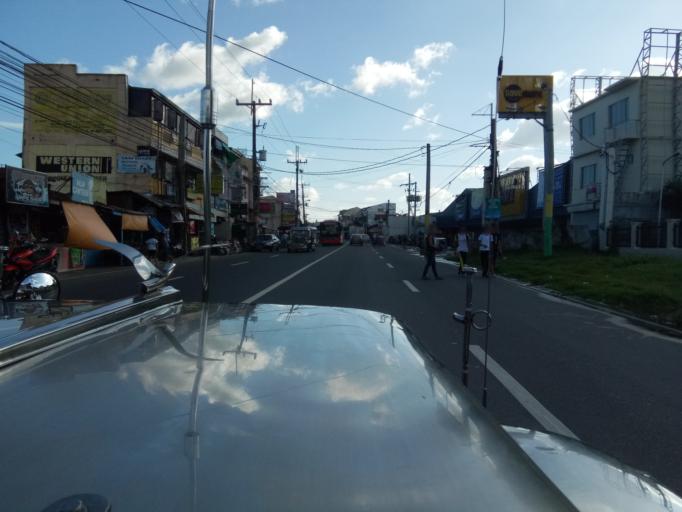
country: PH
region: Calabarzon
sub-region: Province of Cavite
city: Dasmarinas
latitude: 14.3514
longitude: 120.9810
